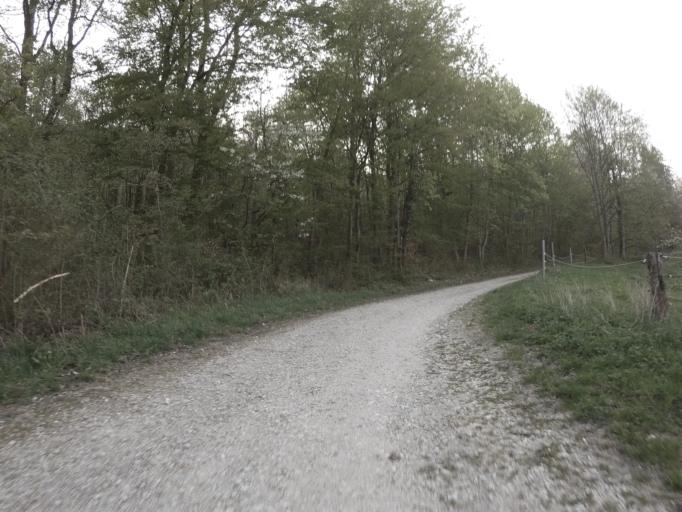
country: DE
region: Baden-Wuerttemberg
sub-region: Tuebingen Region
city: Pfullingen
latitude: 48.4383
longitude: 9.2093
